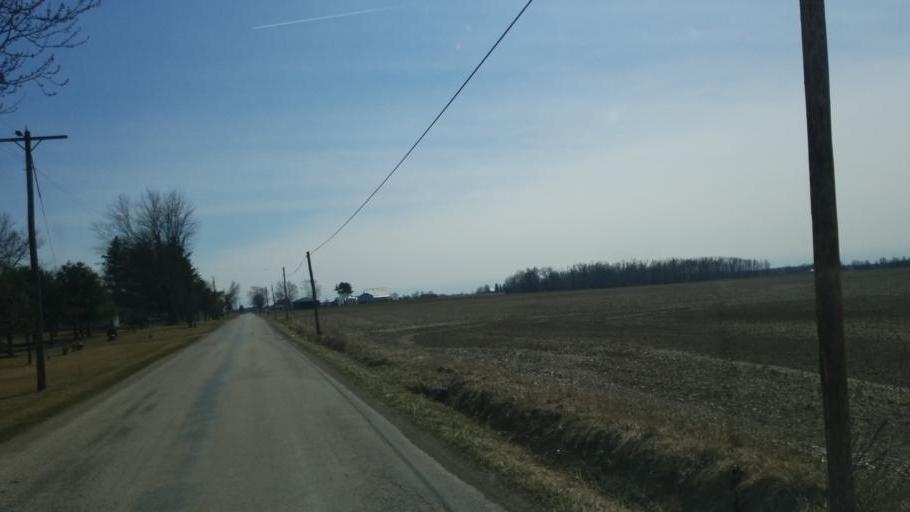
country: US
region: Ohio
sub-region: Morrow County
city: Cardington
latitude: 40.5711
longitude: -82.9192
